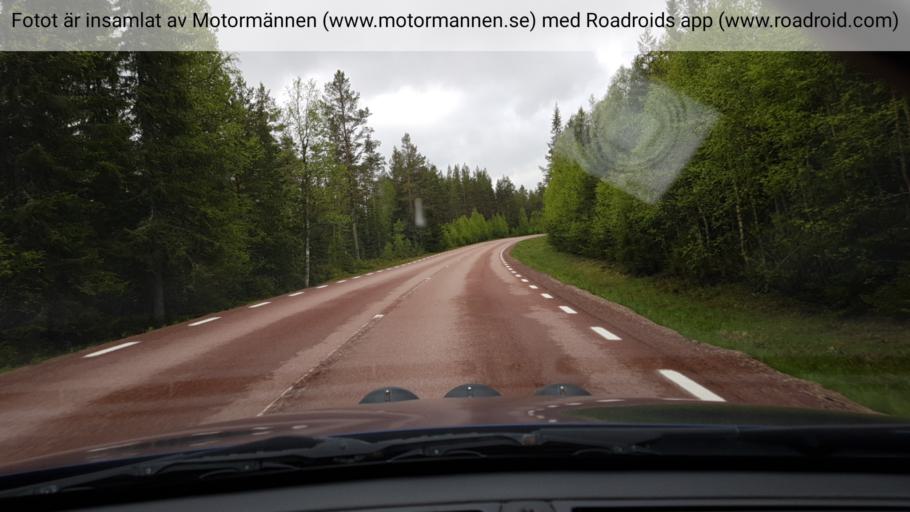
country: SE
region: Dalarna
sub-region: Orsa Kommun
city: Orsa
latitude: 61.2790
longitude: 14.7020
